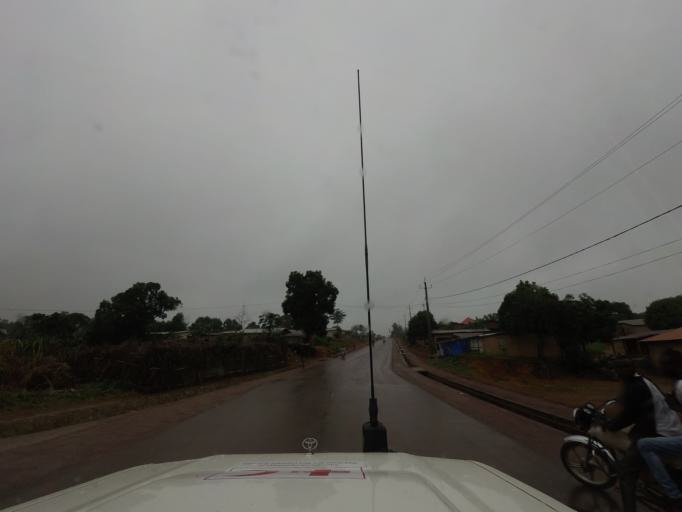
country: GN
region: Nzerekore
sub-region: Nzerekore Prefecture
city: Nzerekore
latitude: 7.7325
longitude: -8.8322
